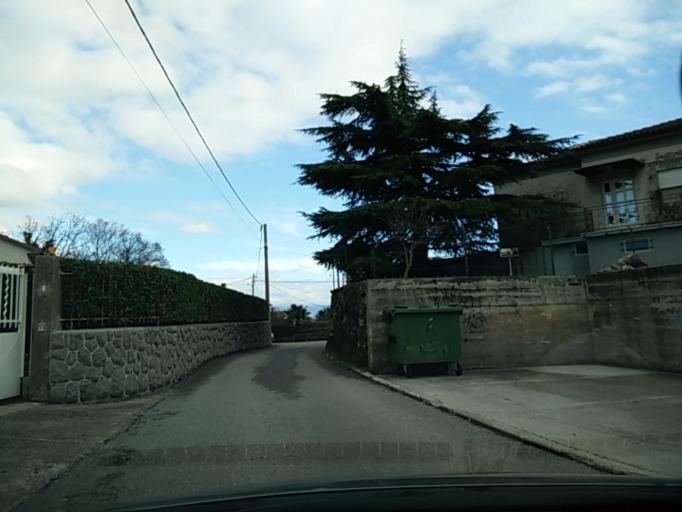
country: HR
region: Primorsko-Goranska
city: Matulji
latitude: 45.3602
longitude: 14.3116
